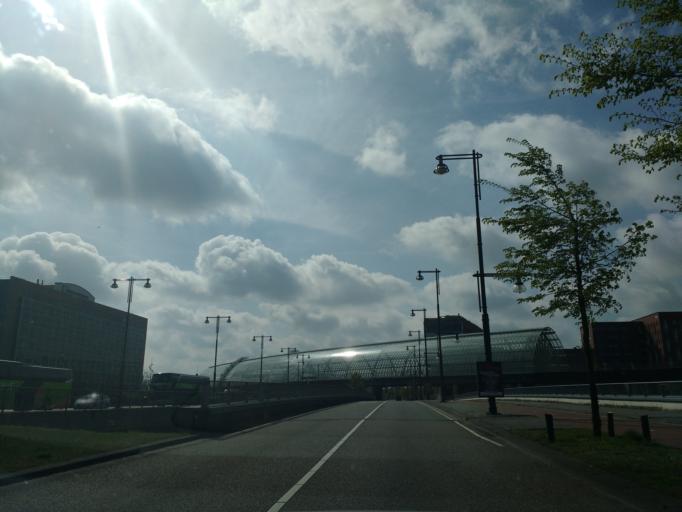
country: NL
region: North Holland
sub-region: Gemeente Zaanstad
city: Zaandam
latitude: 52.3899
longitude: 4.8359
